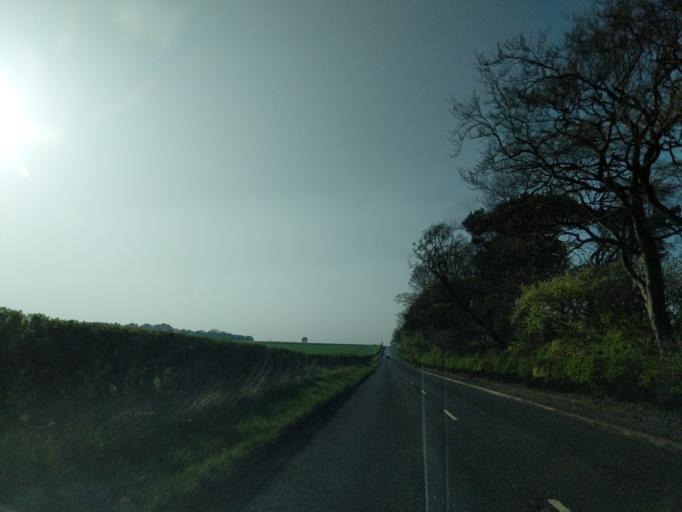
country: GB
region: Scotland
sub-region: Fife
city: Pathhead
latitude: 55.8793
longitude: -3.0128
